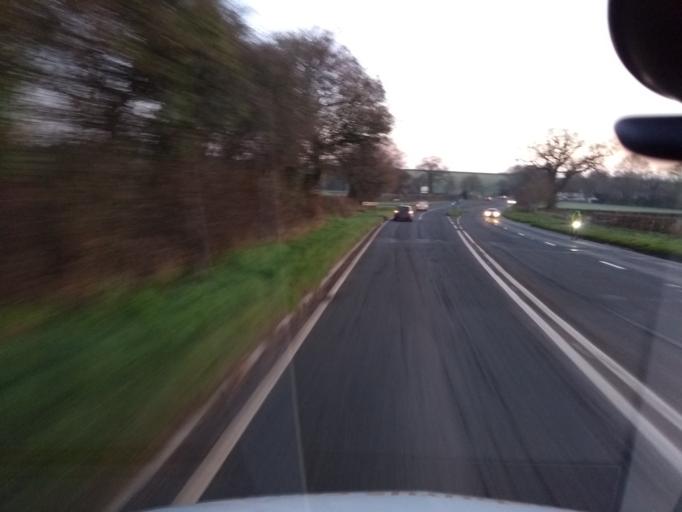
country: GB
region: England
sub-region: Somerset
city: North Petherton
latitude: 51.0622
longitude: -3.0318
